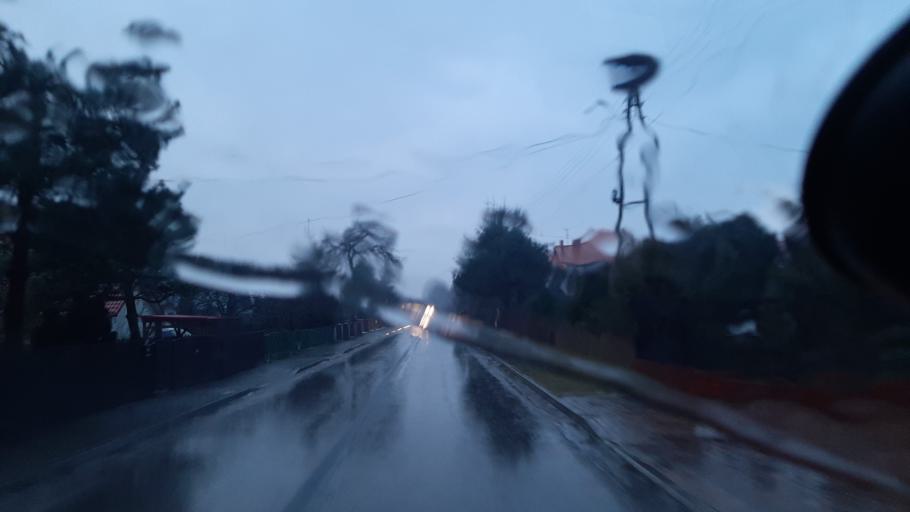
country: PL
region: Lublin Voivodeship
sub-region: Powiat lubartowski
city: Firlej
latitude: 51.5469
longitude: 22.5592
